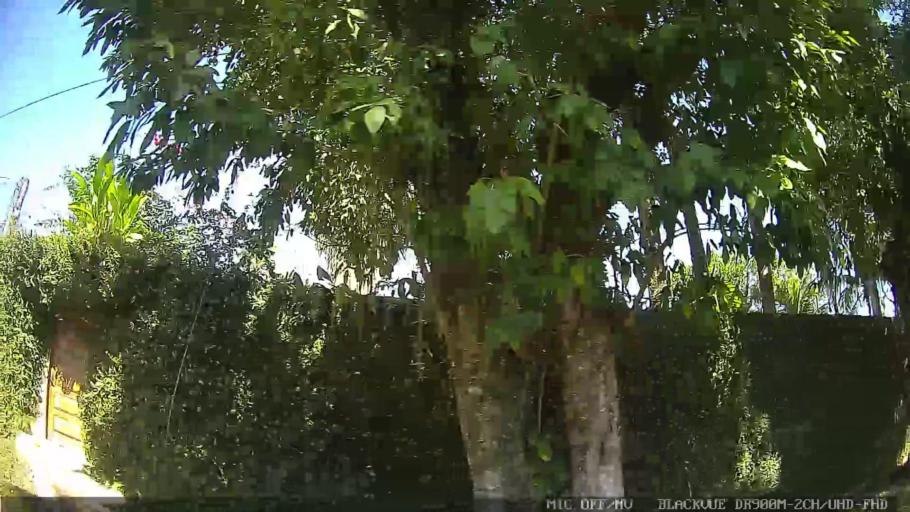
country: BR
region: Sao Paulo
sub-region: Guaruja
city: Guaruja
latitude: -23.9797
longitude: -46.2107
